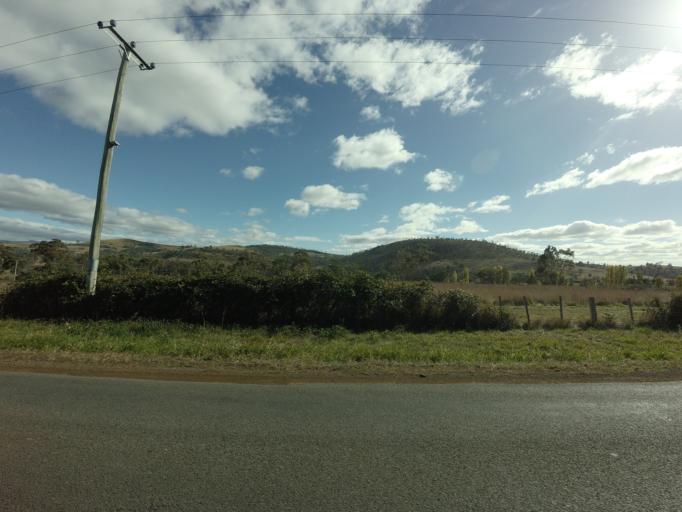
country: AU
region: Tasmania
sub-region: Derwent Valley
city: New Norfolk
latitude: -42.6852
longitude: 146.8464
